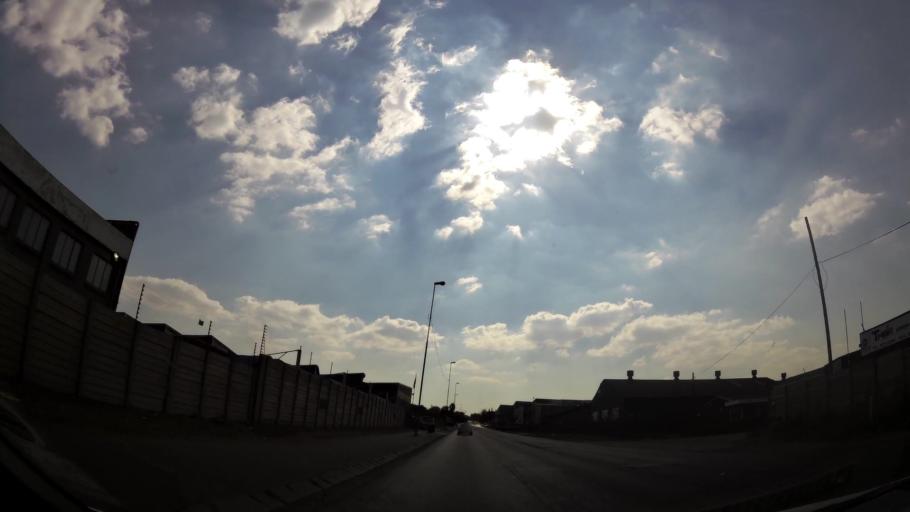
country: ZA
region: Gauteng
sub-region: Ekurhuleni Metropolitan Municipality
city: Boksburg
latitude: -26.1936
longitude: 28.2165
